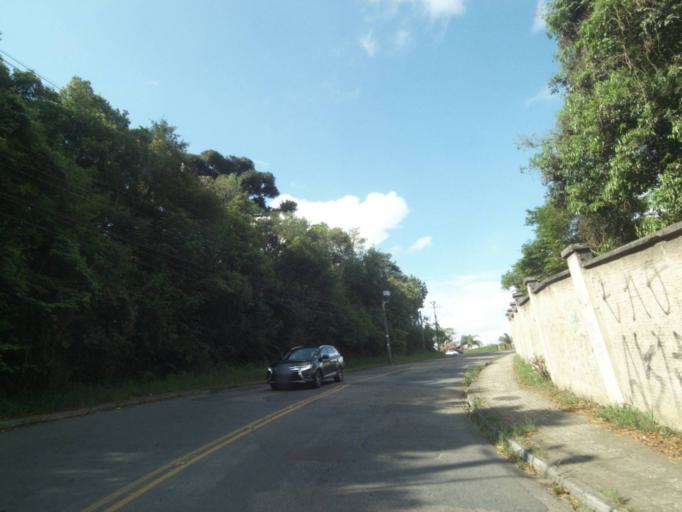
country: BR
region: Parana
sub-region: Curitiba
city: Curitiba
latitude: -25.3849
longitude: -49.3040
